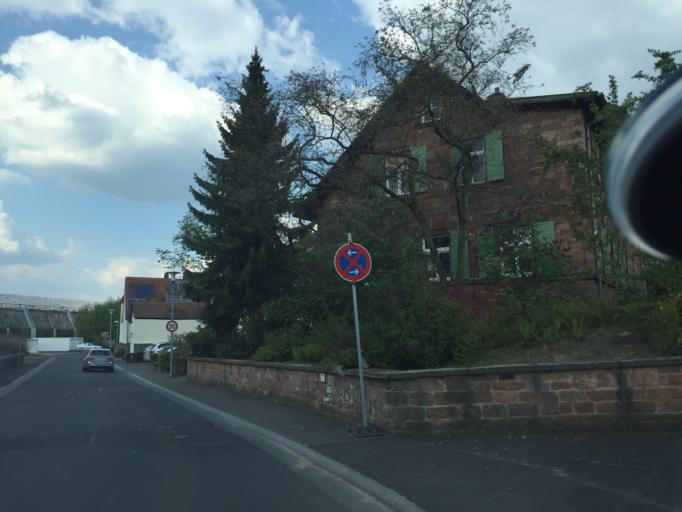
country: DE
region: Bavaria
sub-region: Regierungsbezirk Unterfranken
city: Hosbach
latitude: 49.9983
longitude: 9.2019
